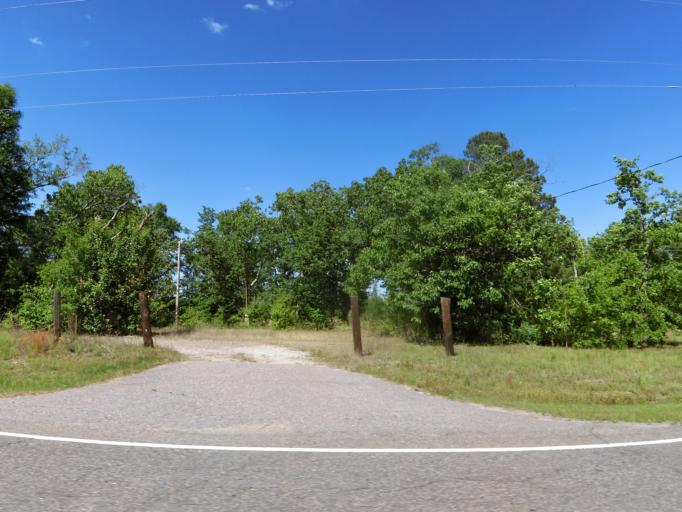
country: US
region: South Carolina
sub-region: Barnwell County
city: Williston
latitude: 33.4789
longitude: -81.5103
